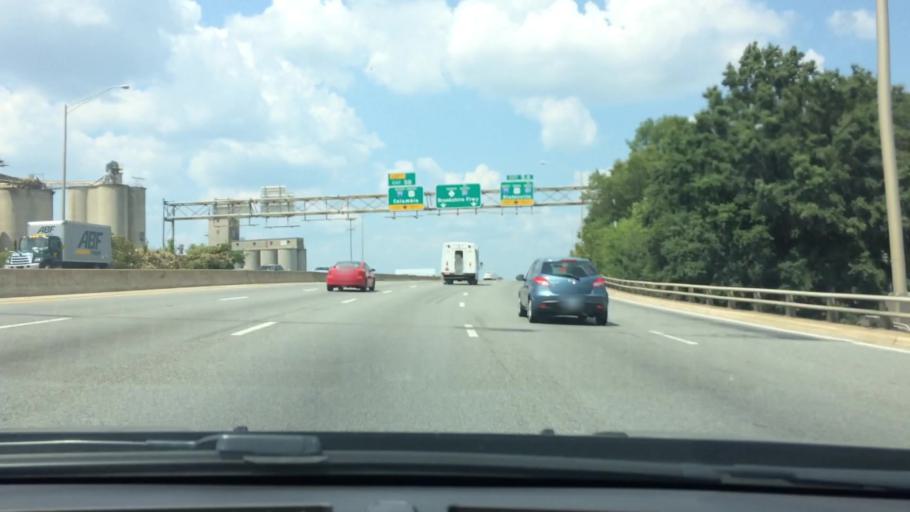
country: US
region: North Carolina
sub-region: Mecklenburg County
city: Charlotte
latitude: 35.2359
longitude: -80.8392
